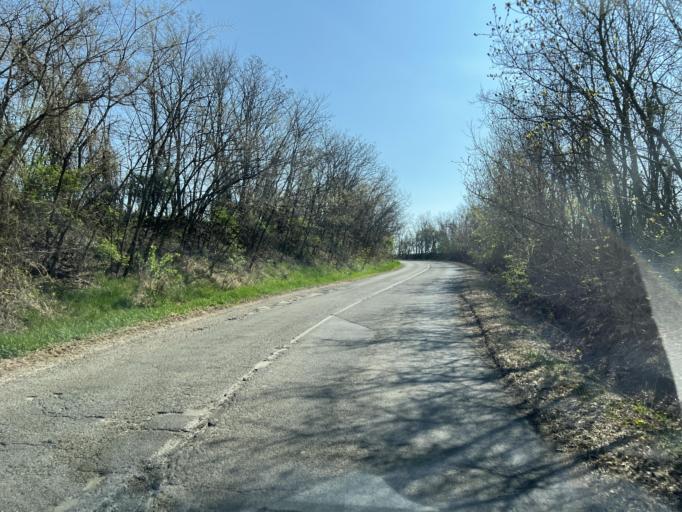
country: HU
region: Pest
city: Orbottyan
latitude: 47.7393
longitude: 19.2968
